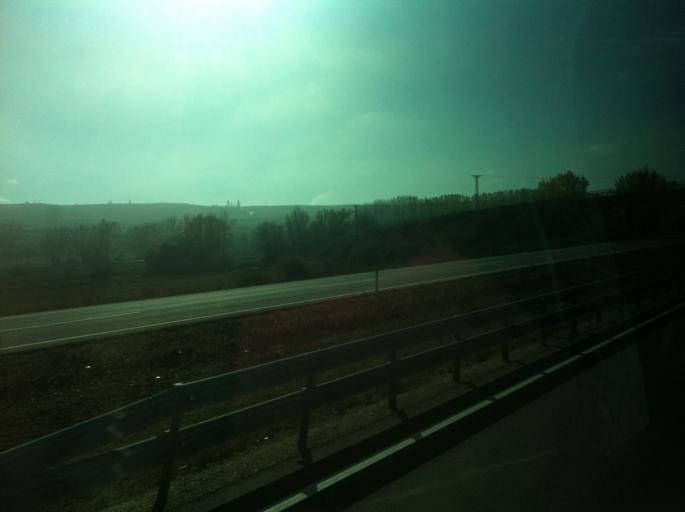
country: ES
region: Castille and Leon
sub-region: Provincia de Burgos
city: Rubena
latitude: 42.3951
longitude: -3.5690
